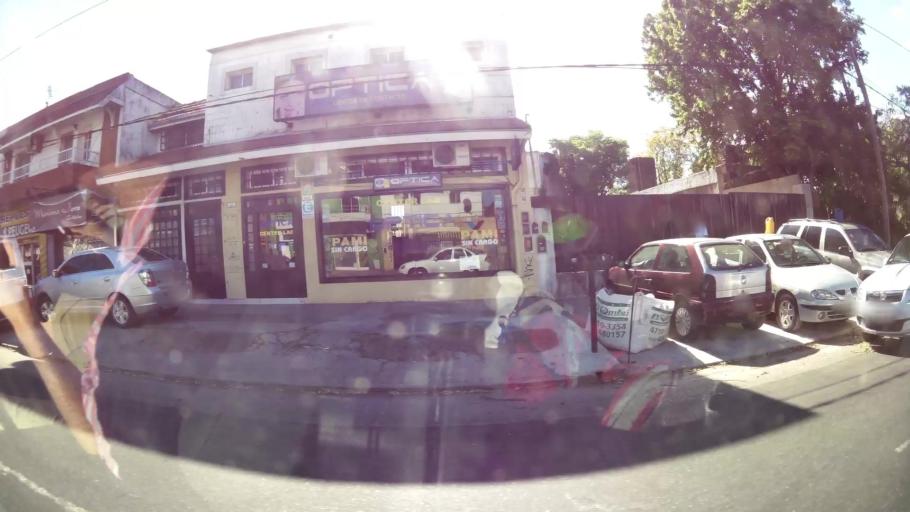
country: AR
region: Buenos Aires
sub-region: Partido de General San Martin
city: General San Martin
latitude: -34.5151
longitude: -58.5682
